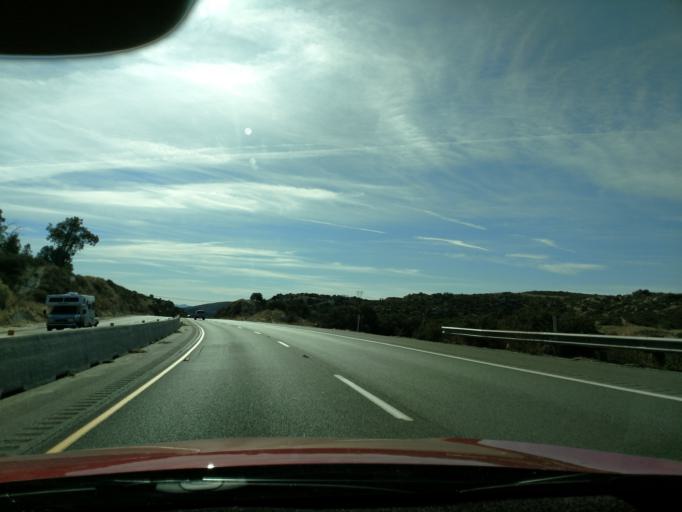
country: US
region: California
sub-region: Riverside County
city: Beaumont
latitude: 33.9046
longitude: -116.9848
